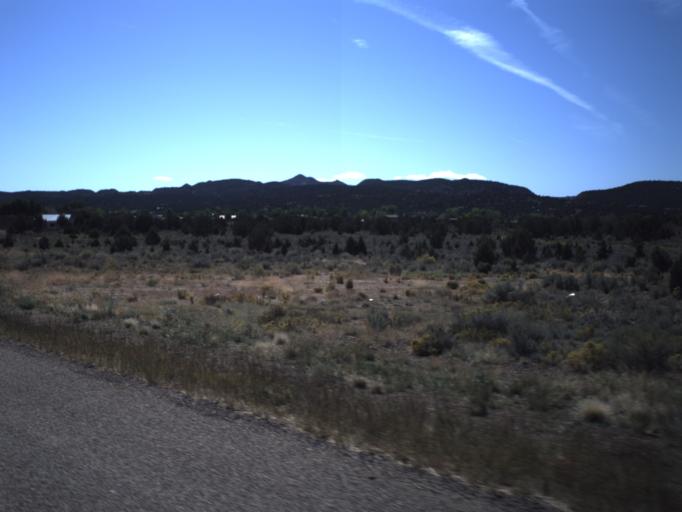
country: US
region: Utah
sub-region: Washington County
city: Ivins
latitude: 37.3127
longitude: -113.6758
